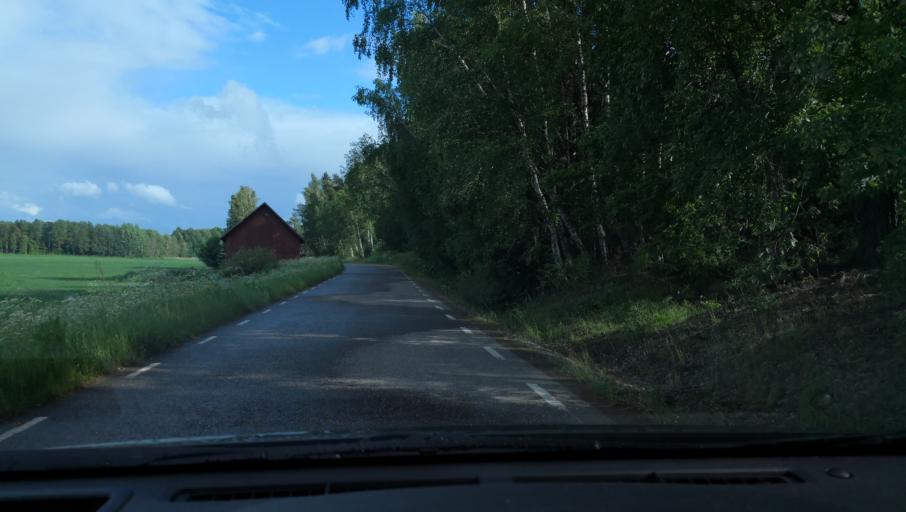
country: SE
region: OErebro
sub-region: Lindesbergs Kommun
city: Fellingsbro
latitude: 59.3101
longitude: 15.6780
